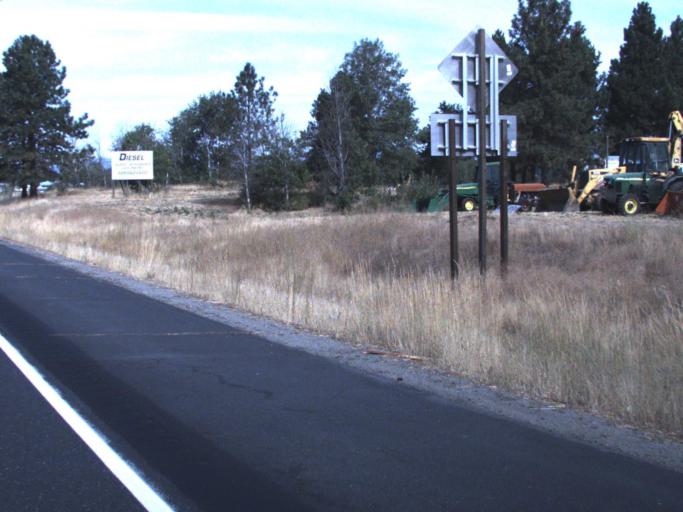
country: US
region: Washington
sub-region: Spokane County
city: Deer Park
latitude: 47.9344
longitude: -117.4694
